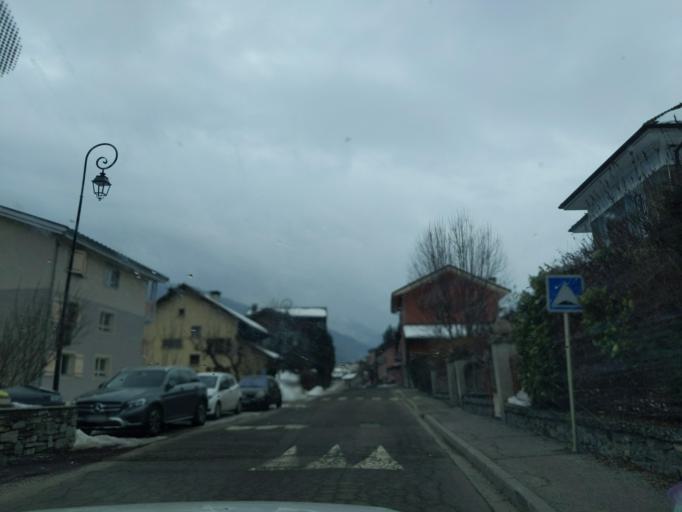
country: FR
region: Rhone-Alpes
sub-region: Departement de la Savoie
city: Bourg-Saint-Maurice
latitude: 45.6209
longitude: 6.7693
